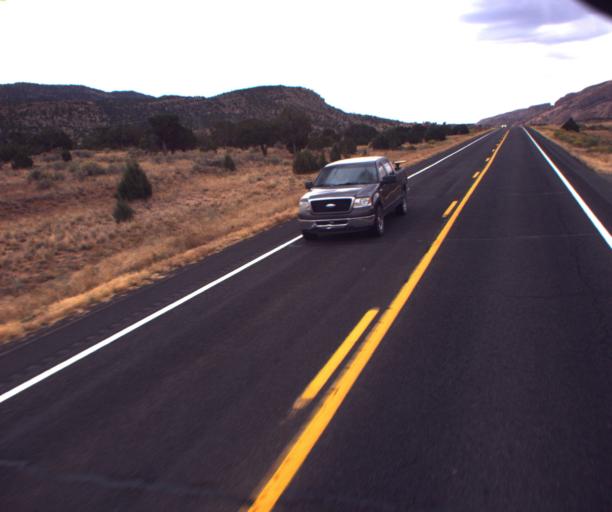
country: US
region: Arizona
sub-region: Navajo County
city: Kayenta
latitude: 36.6789
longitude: -110.3896
